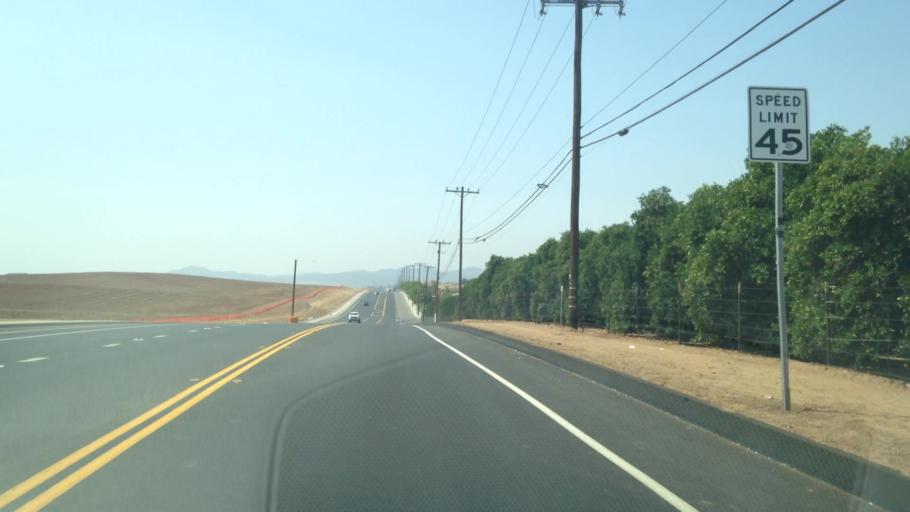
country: US
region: California
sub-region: Riverside County
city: Woodcrest
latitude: 33.8871
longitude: -117.3139
